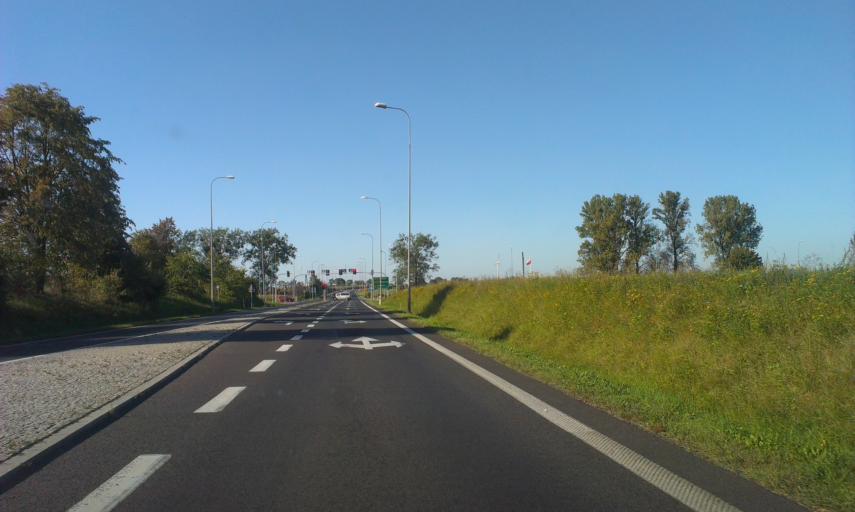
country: PL
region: Kujawsko-Pomorskie
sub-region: Powiat torunski
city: Chelmza
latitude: 53.1796
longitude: 18.5679
